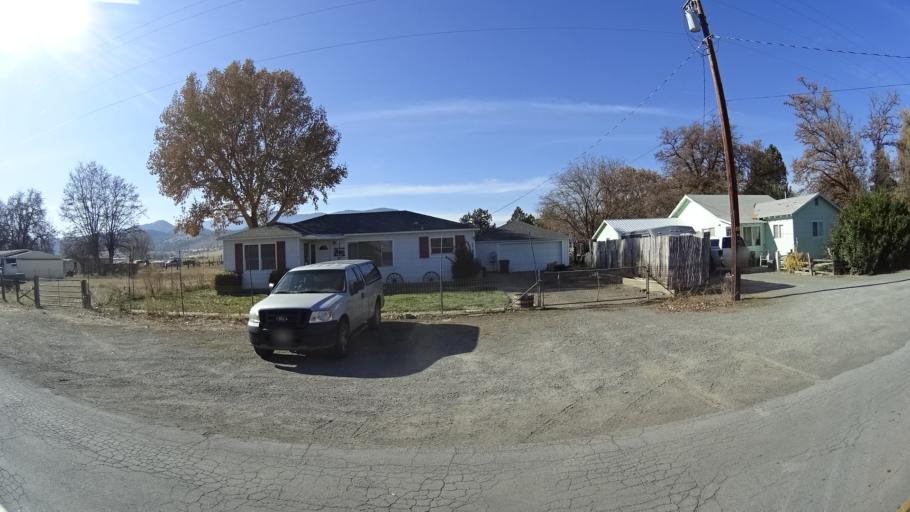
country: US
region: California
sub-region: Siskiyou County
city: Montague
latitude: 41.6428
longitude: -122.5224
